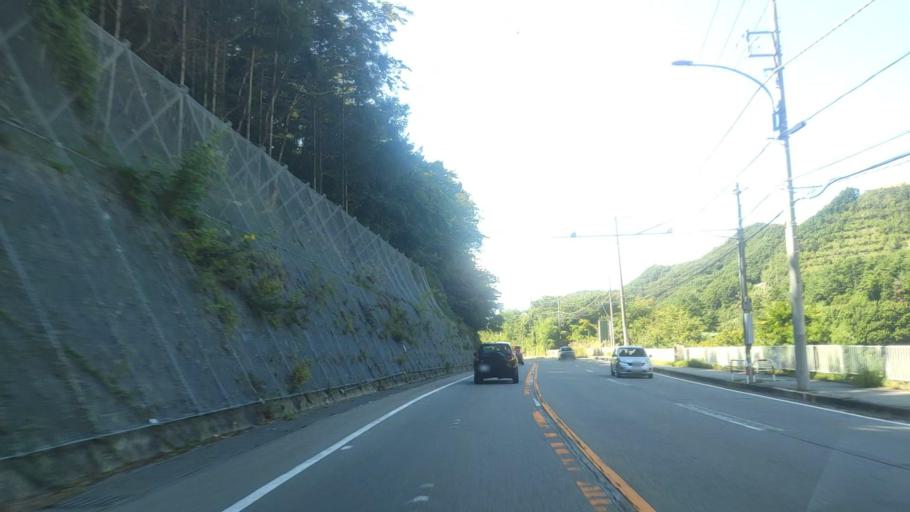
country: JP
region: Yamanashi
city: Fujikawaguchiko
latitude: 35.5886
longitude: 138.7346
